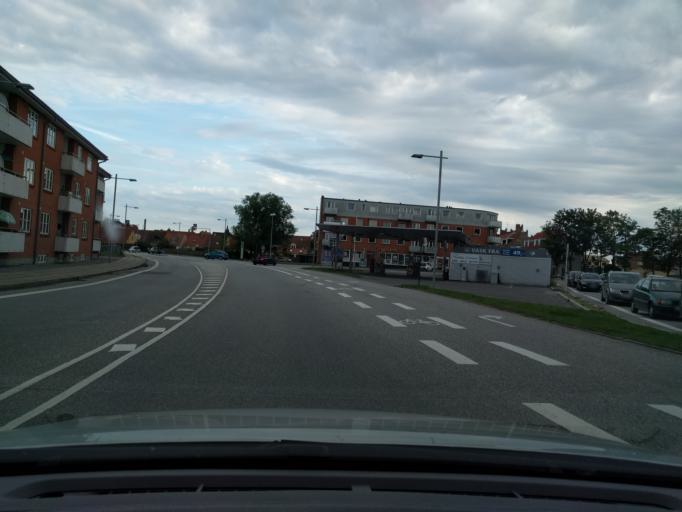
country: DK
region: Zealand
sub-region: Guldborgsund Kommune
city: Nykobing Falster
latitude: 54.7726
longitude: 11.8667
